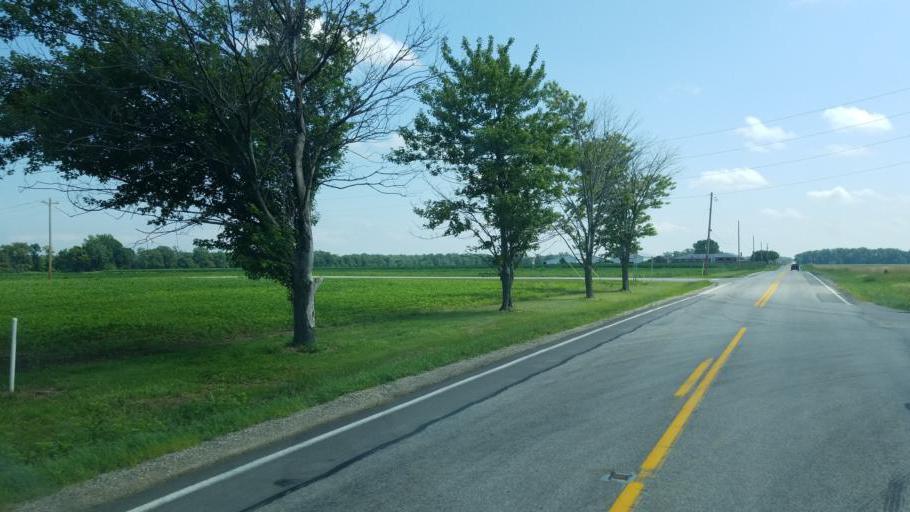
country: US
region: Ohio
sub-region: Huron County
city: Bellevue
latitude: 41.2261
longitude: -82.8390
